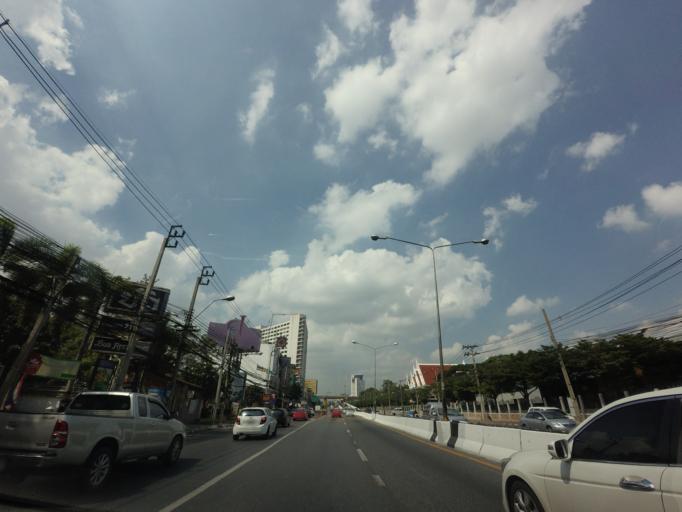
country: TH
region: Bangkok
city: Chatuchak
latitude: 13.8456
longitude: 100.5650
